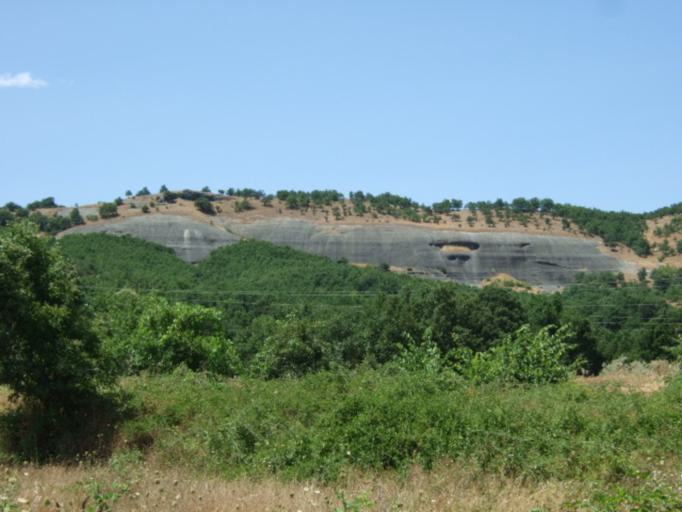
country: GR
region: Thessaly
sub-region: Trikala
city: Kastraki
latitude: 39.7321
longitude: 21.5755
